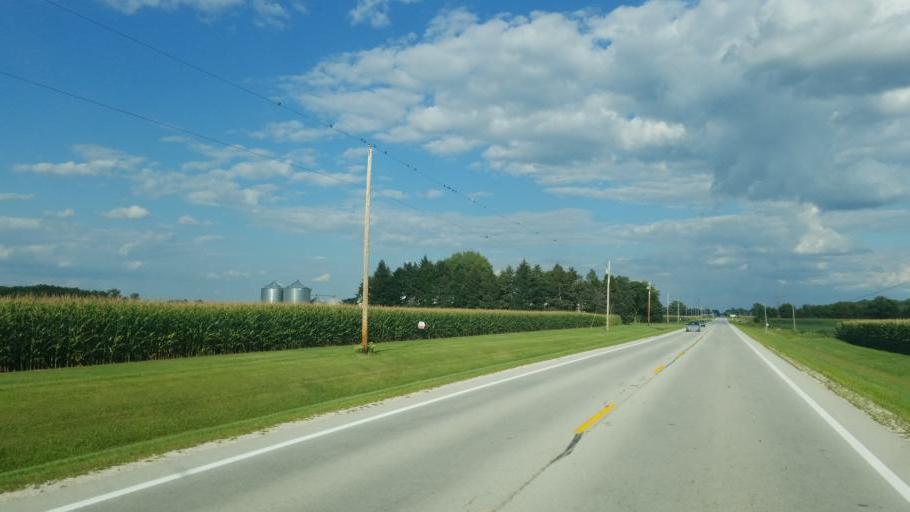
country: US
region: Ohio
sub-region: Sandusky County
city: Gibsonburg
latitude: 41.3413
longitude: -83.3996
